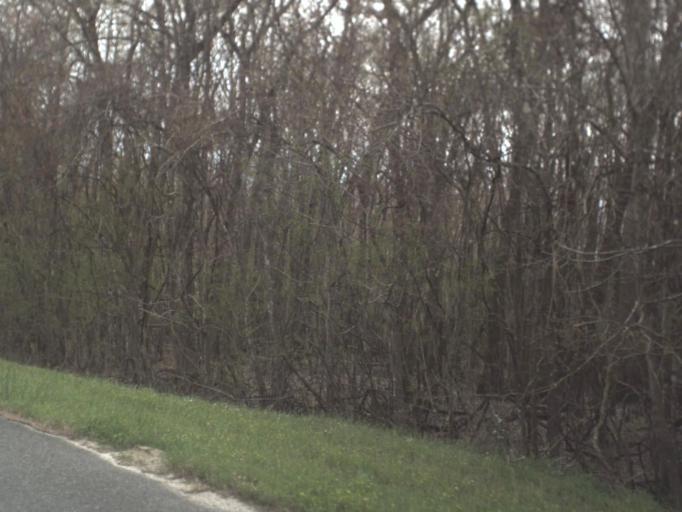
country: US
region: Florida
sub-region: Wakulla County
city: Crawfordville
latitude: 30.2459
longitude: -84.3166
